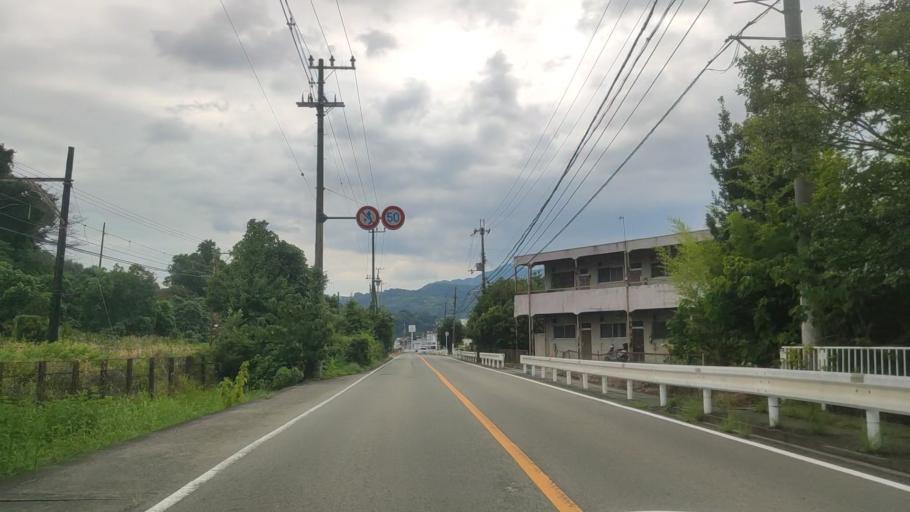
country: JP
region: Wakayama
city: Hashimoto
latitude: 34.2953
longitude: 135.5760
